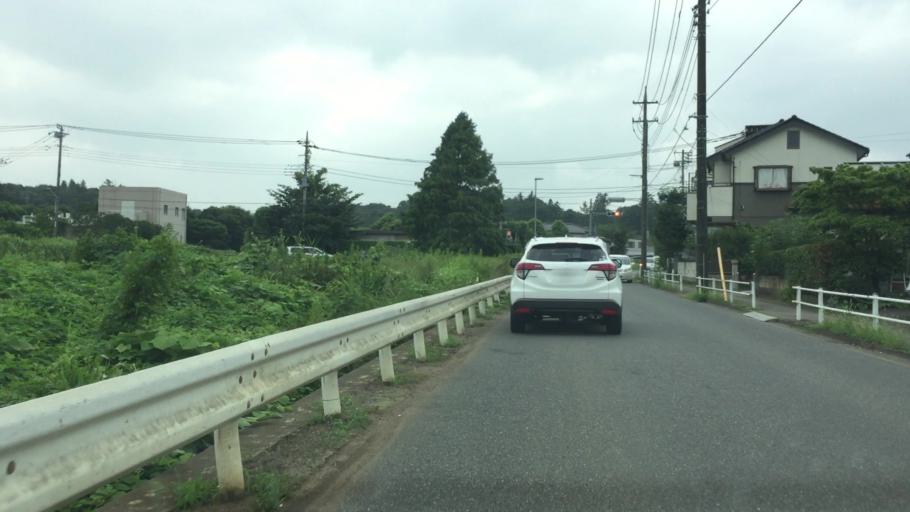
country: JP
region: Chiba
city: Kashiwa
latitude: 35.8185
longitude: 139.9879
